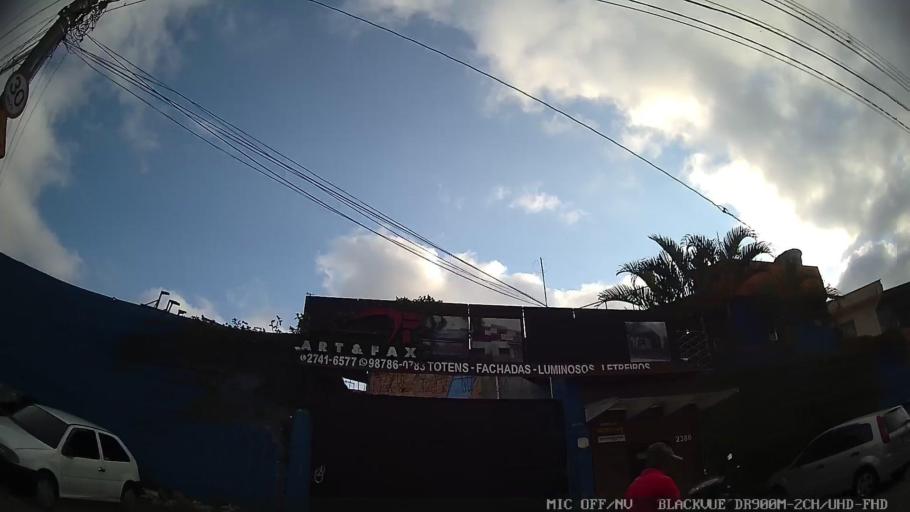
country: BR
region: Sao Paulo
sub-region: Guarulhos
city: Guarulhos
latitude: -23.5462
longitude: -46.5053
